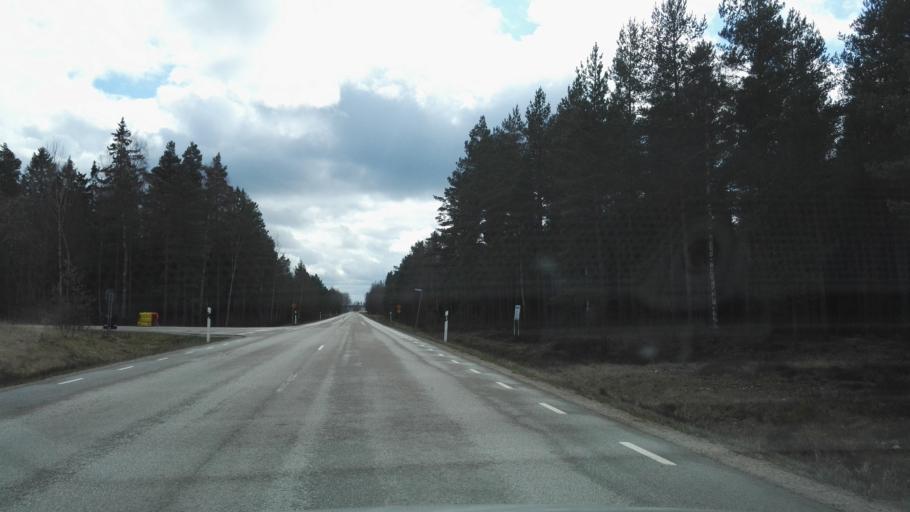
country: SE
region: Kronoberg
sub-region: Vaxjo Kommun
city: Vaexjoe
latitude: 56.9236
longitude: 14.7340
